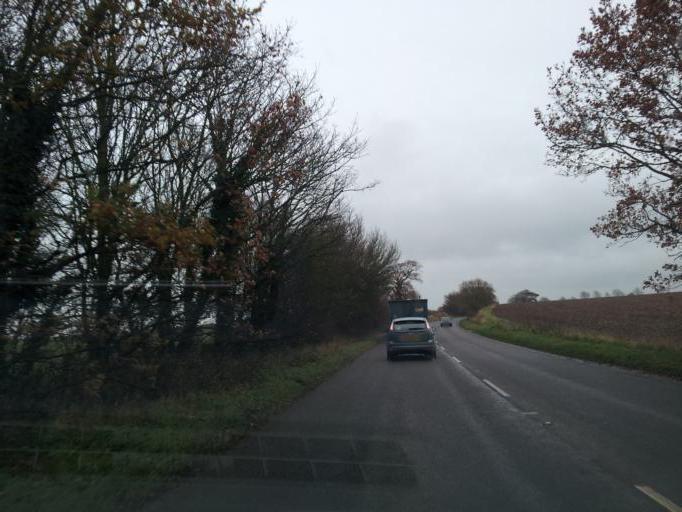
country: GB
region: England
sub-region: Norfolk
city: Martham
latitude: 52.6967
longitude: 1.6069
